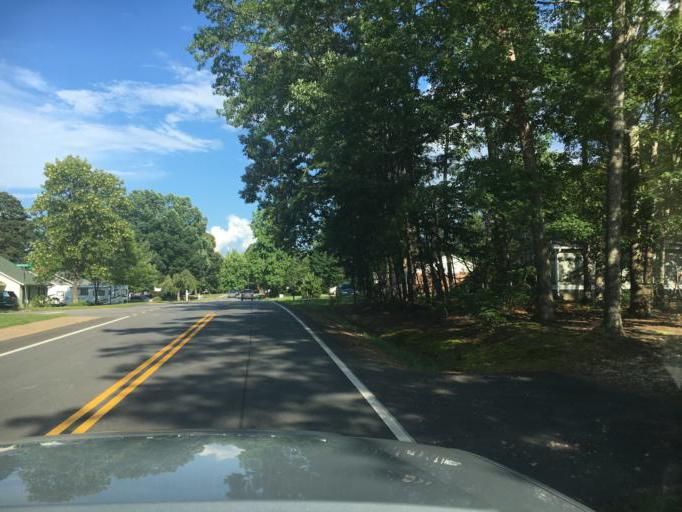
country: US
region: South Carolina
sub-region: Greenville County
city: Mauldin
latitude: 34.7786
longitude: -82.2848
